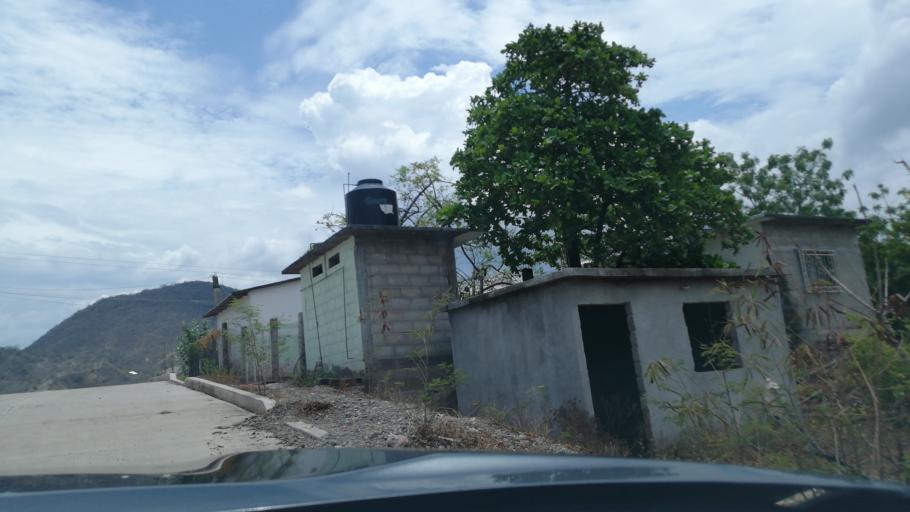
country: MX
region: Oaxaca
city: Santa Maria Jalapa del Marques
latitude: 16.4441
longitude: -95.4401
